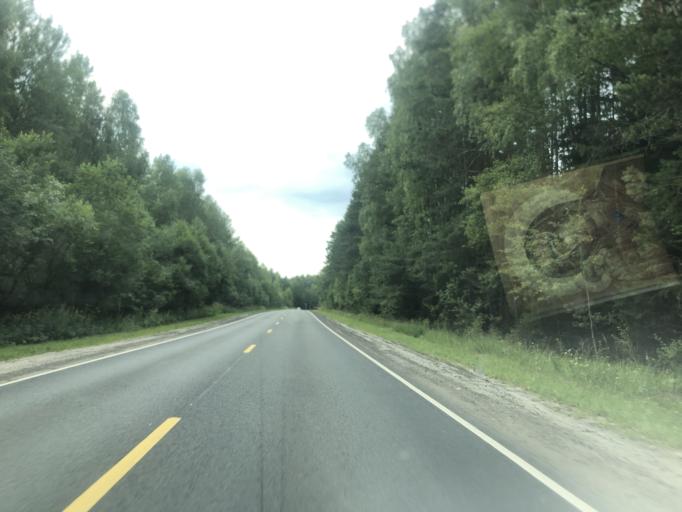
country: RU
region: Ivanovo
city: Verkhniy Landekh
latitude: 56.7398
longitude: 42.5348
